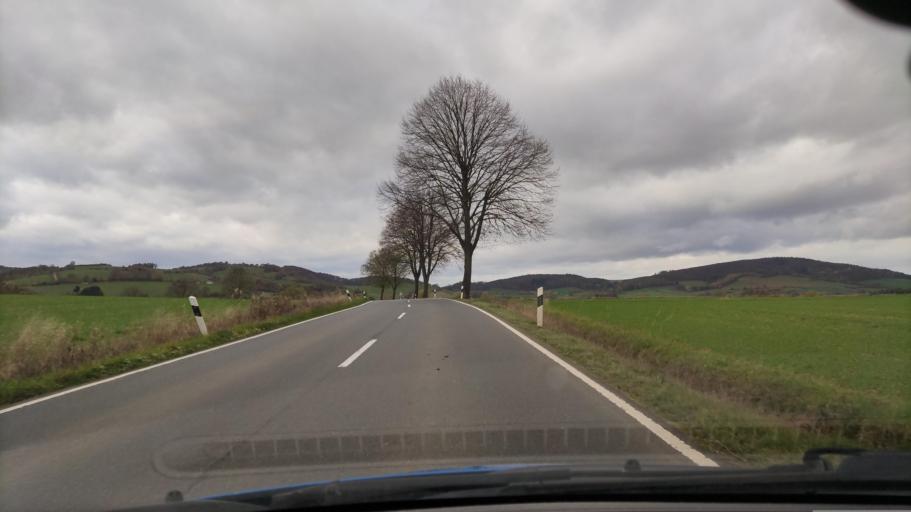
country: DE
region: Lower Saxony
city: Wangelnstedt
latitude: 51.8678
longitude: 9.6994
